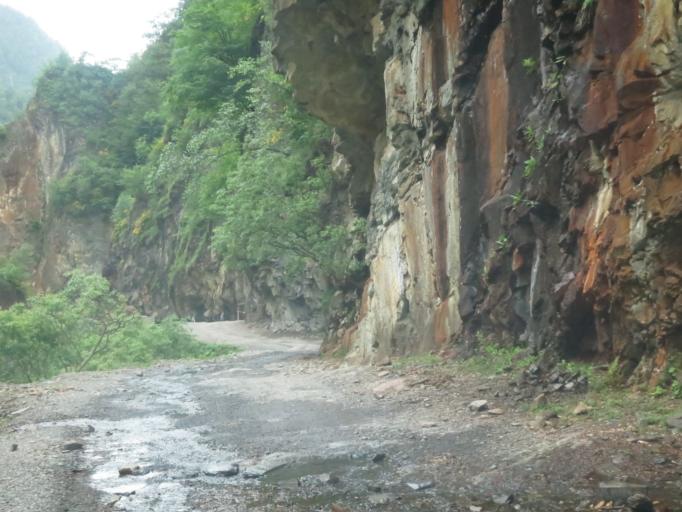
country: GE
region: Kakheti
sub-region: Telavi
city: Telavi
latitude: 42.2400
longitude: 45.4933
